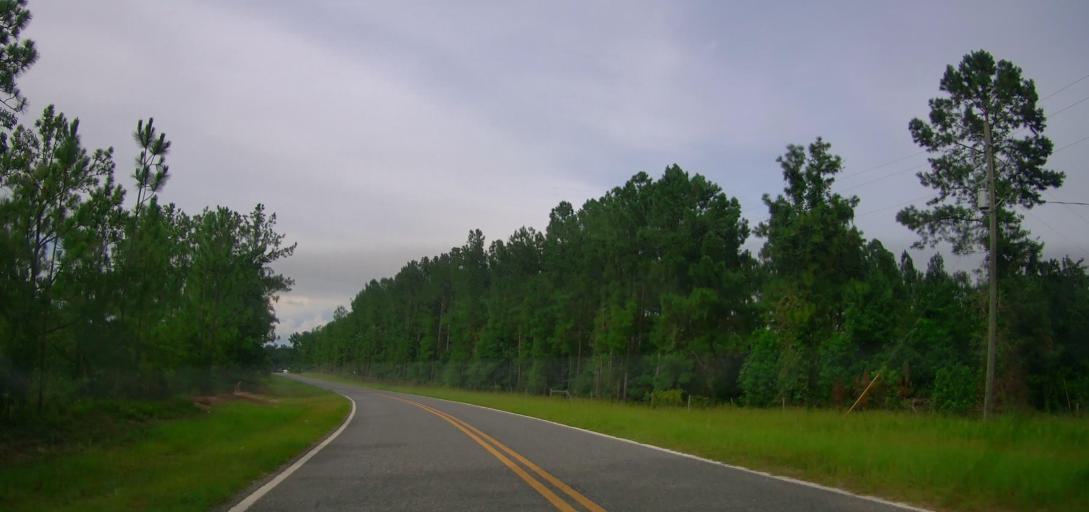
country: US
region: Georgia
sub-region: Wayne County
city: Jesup
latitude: 31.6711
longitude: -81.9083
